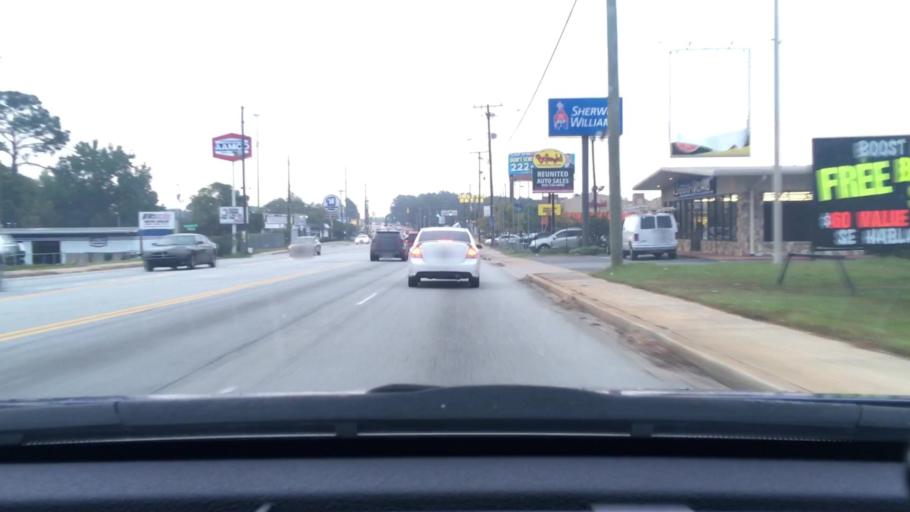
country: US
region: South Carolina
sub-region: Lexington County
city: Saint Andrews
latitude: 34.0433
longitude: -81.0986
